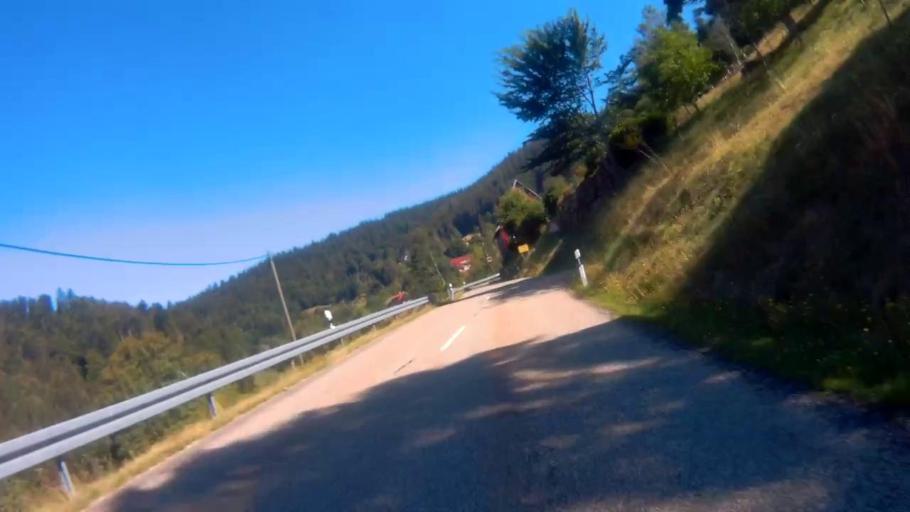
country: DE
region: Baden-Wuerttemberg
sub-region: Freiburg Region
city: Badenweiler
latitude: 47.7629
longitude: 7.7531
